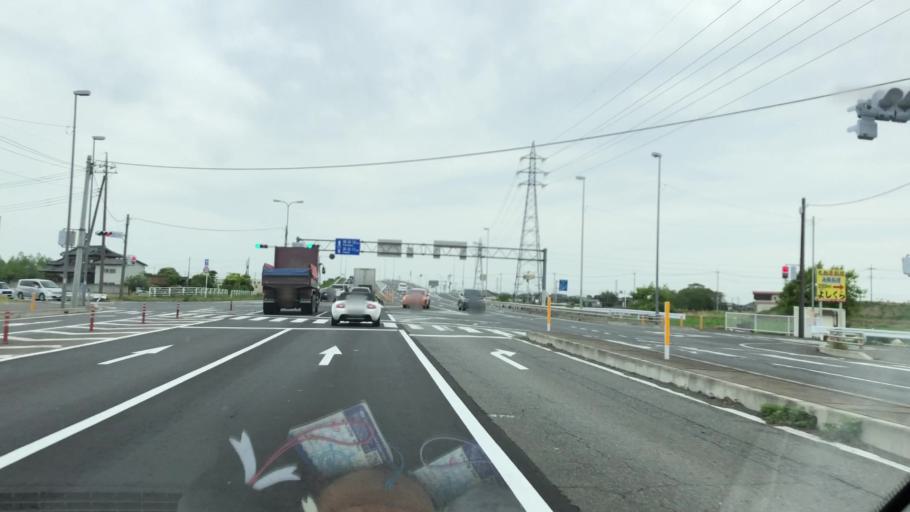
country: JP
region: Gunma
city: Sakai-nakajima
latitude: 36.2638
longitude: 139.2956
